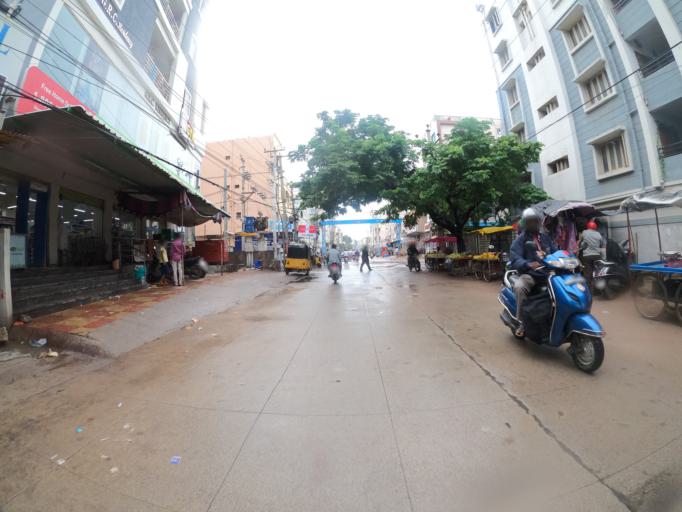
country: IN
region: Telangana
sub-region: Rangareddi
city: Kukatpalli
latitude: 17.4580
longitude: 78.4038
